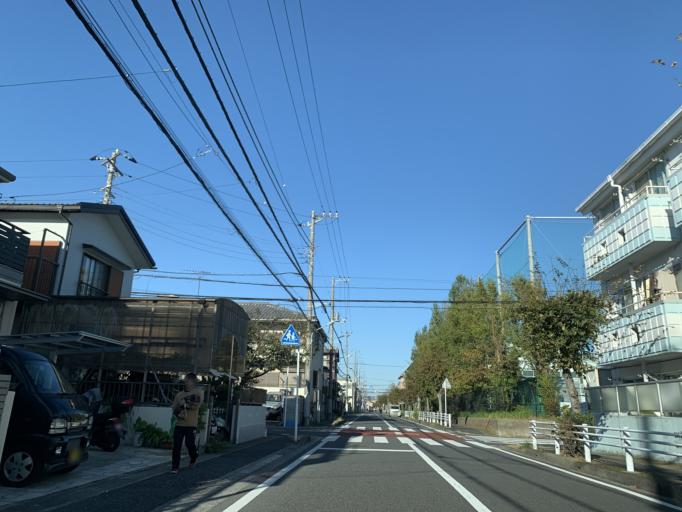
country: JP
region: Tokyo
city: Urayasu
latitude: 35.6500
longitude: 139.8882
